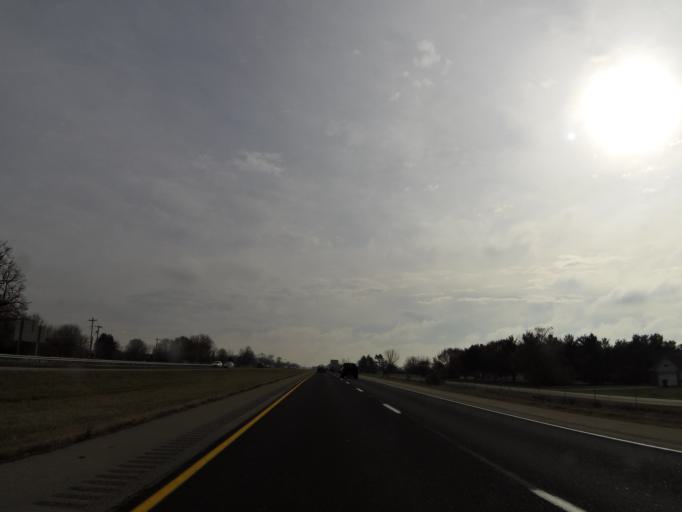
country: US
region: Indiana
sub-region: Hancock County
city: New Palestine
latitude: 39.6423
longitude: -85.9088
